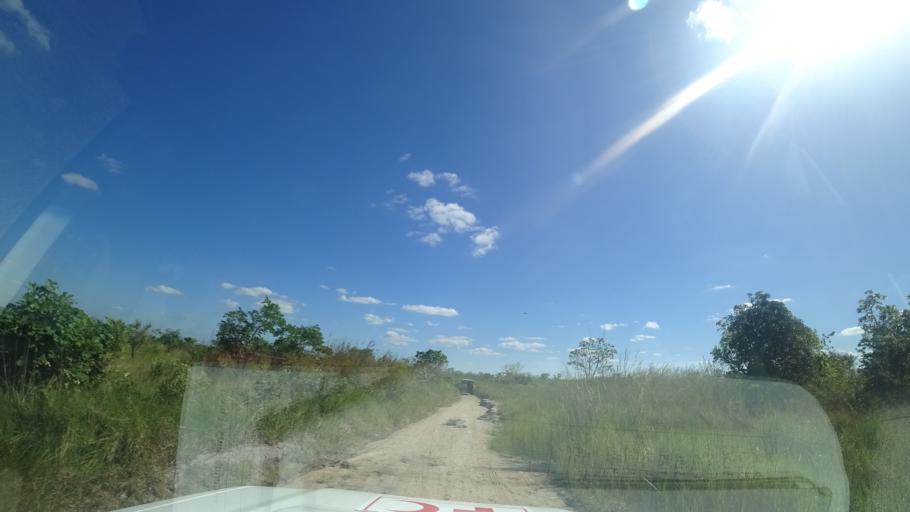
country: MZ
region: Sofala
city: Dondo
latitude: -19.4771
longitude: 34.6283
